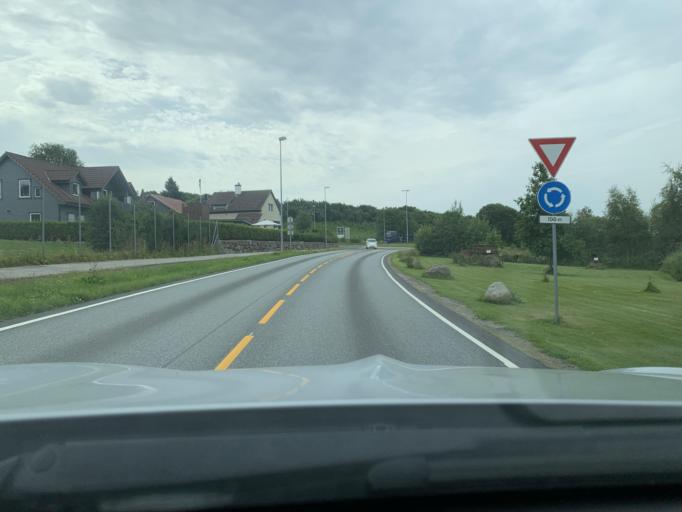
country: NO
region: Rogaland
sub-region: Sandnes
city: Sandnes
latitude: 58.7722
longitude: 5.7254
